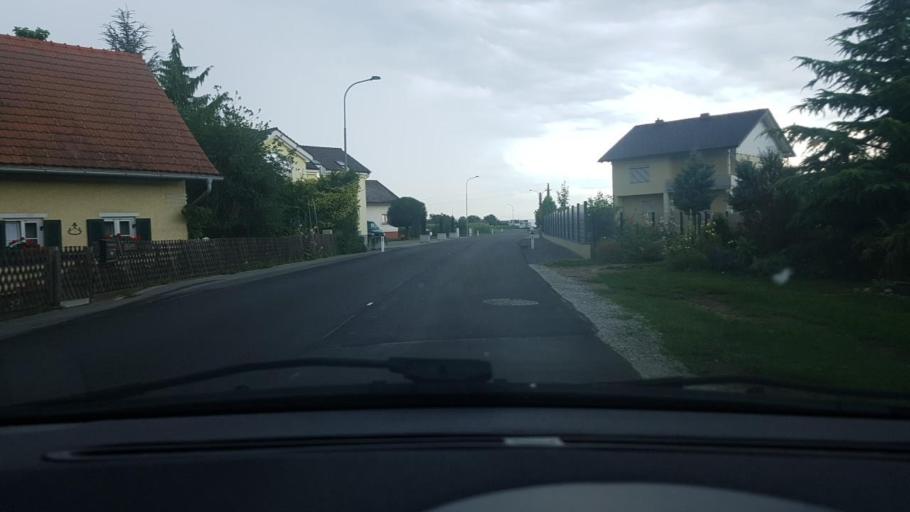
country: AT
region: Styria
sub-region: Politischer Bezirk Graz-Umgebung
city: Wundschuh
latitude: 46.9393
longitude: 15.4446
